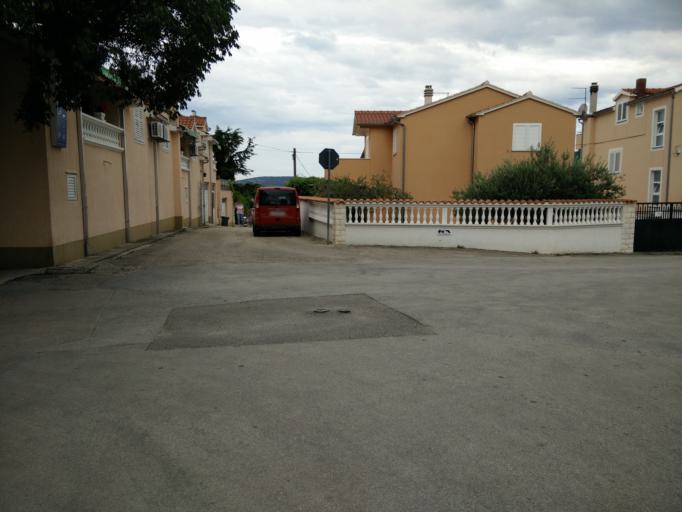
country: HR
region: Sibensko-Kniniska
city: Vodice
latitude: 43.7559
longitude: 15.7707
